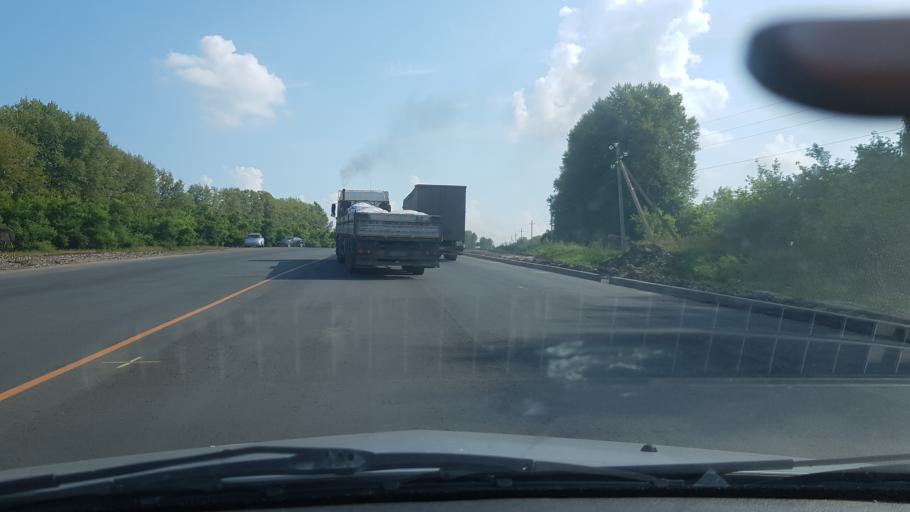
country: RU
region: Chuvashia
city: Tsivil'sk
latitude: 55.7303
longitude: 47.4480
